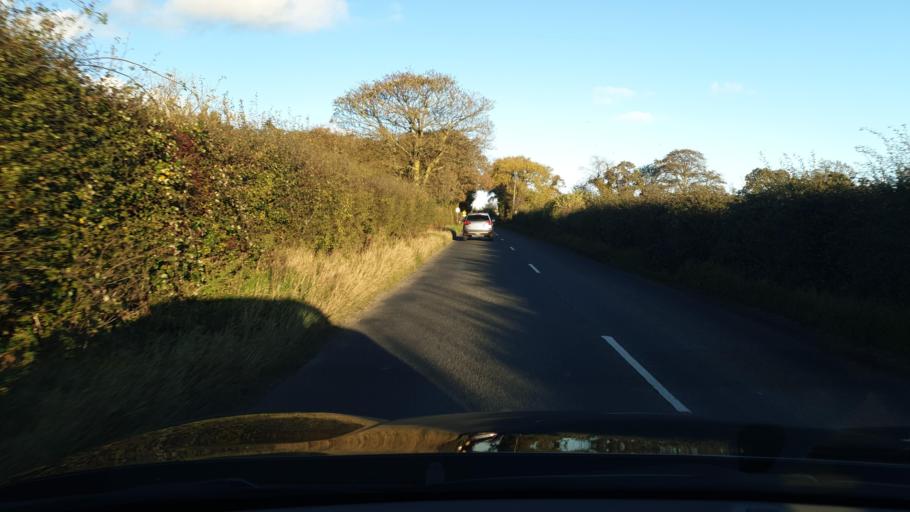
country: IE
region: Leinster
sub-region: Lu
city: Drogheda
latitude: 53.6965
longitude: -6.3215
